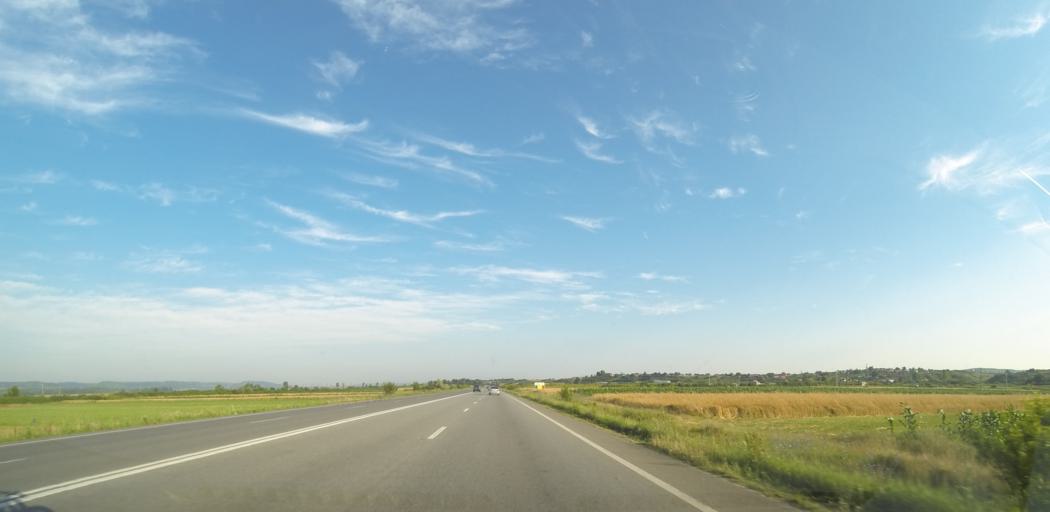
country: RO
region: Dolj
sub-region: Comuna Filiasi
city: Racarii de Sus
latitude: 44.5256
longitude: 23.5602
